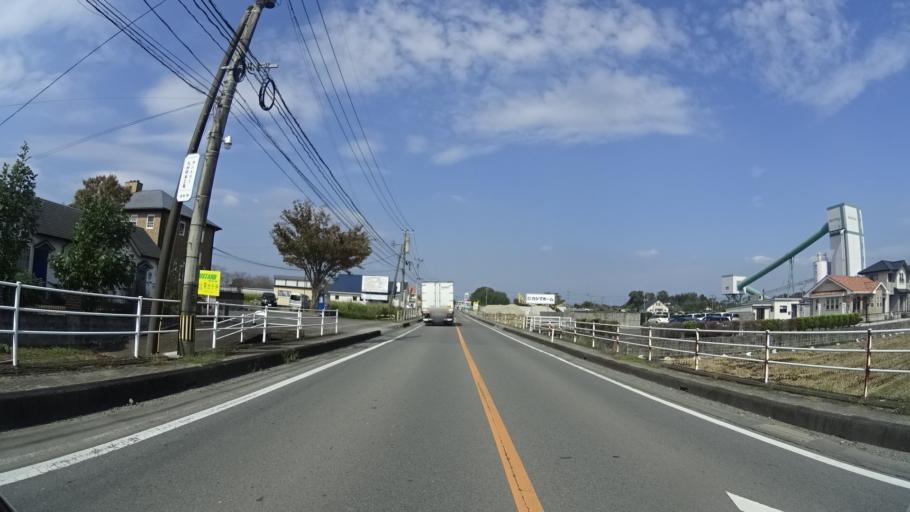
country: JP
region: Kumamoto
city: Kumamoto
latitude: 32.7432
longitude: 130.7714
